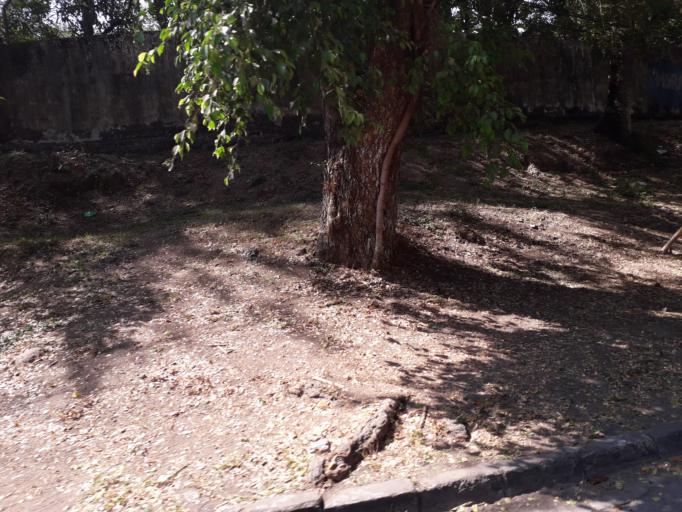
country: ID
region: Daerah Istimewa Yogyakarta
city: Yogyakarta
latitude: -7.7665
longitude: 110.3749
